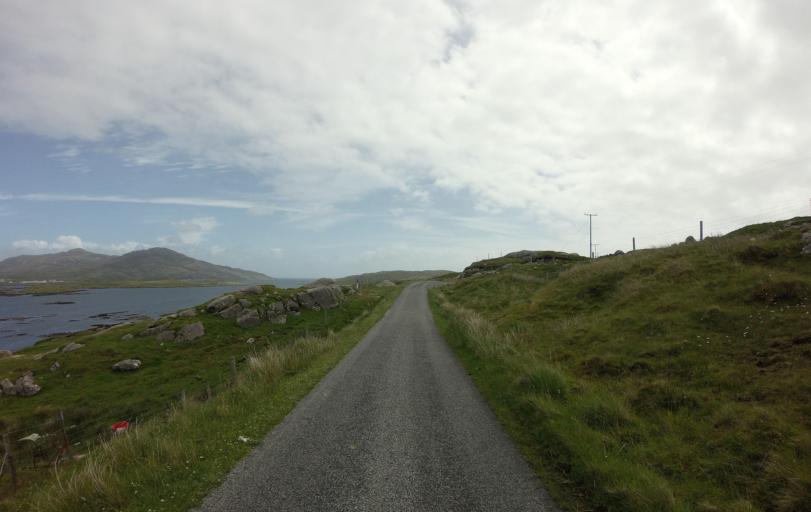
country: GB
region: Scotland
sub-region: Eilean Siar
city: Isle of South Uist
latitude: 57.1370
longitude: -7.3252
